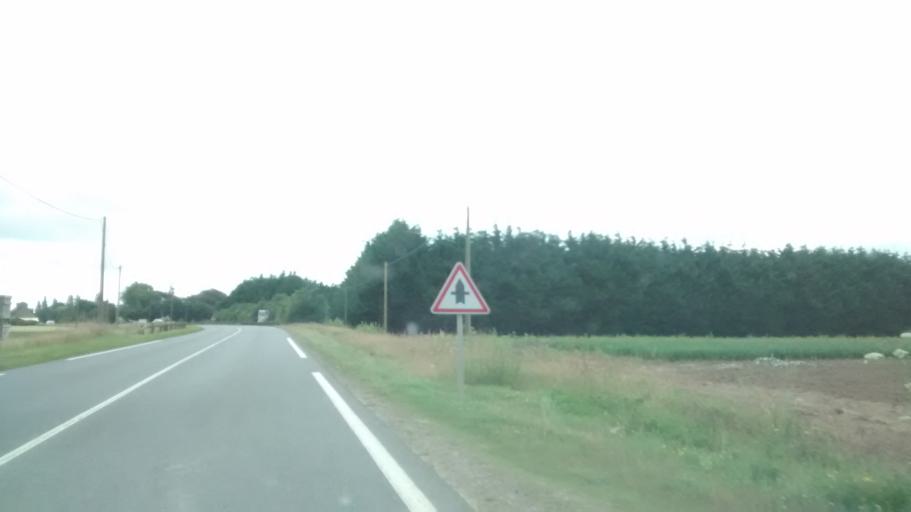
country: FR
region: Brittany
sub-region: Departement d'Ille-et-Vilaine
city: Saint-Meloir-des-Ondes
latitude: 48.6338
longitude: -1.9346
